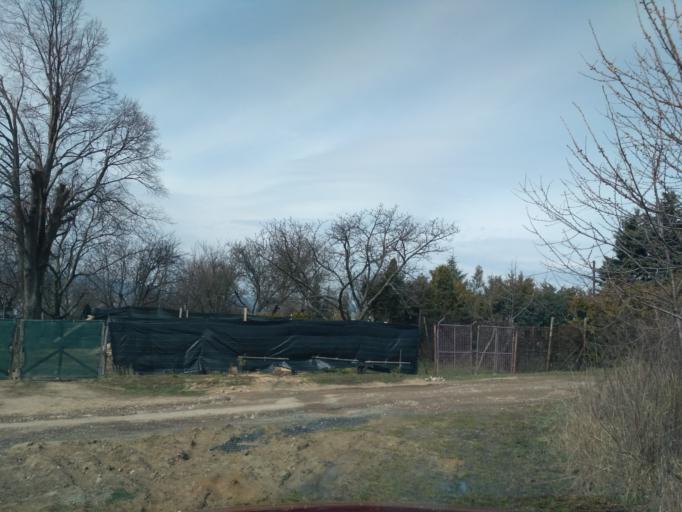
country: SK
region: Kosicky
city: Kosice
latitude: 48.7092
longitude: 21.2890
